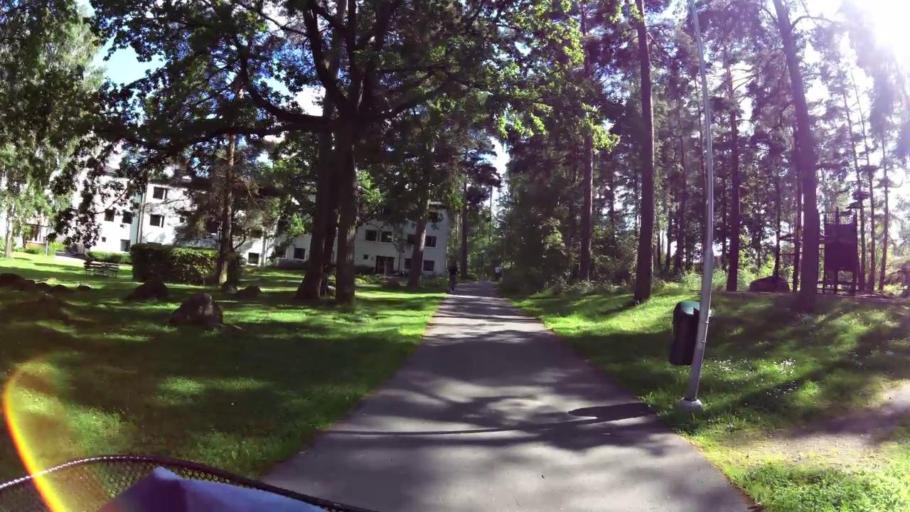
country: SE
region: OEstergoetland
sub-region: Linkopings Kommun
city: Linkoping
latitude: 58.3937
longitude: 15.6584
